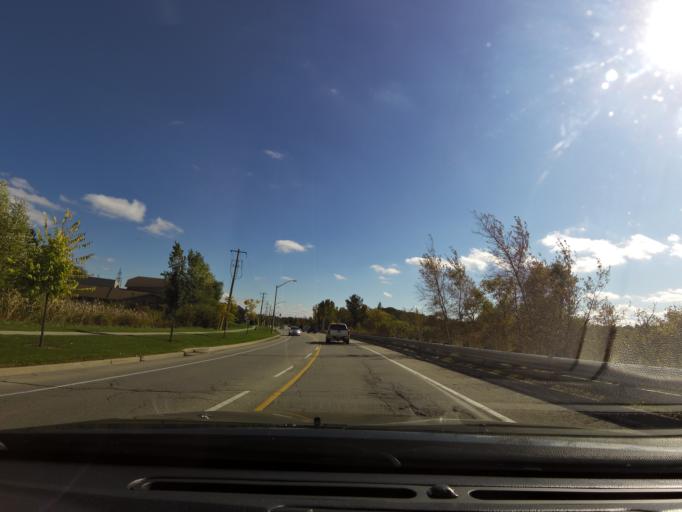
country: CA
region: Ontario
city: Ancaster
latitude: 43.2254
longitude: -79.9359
